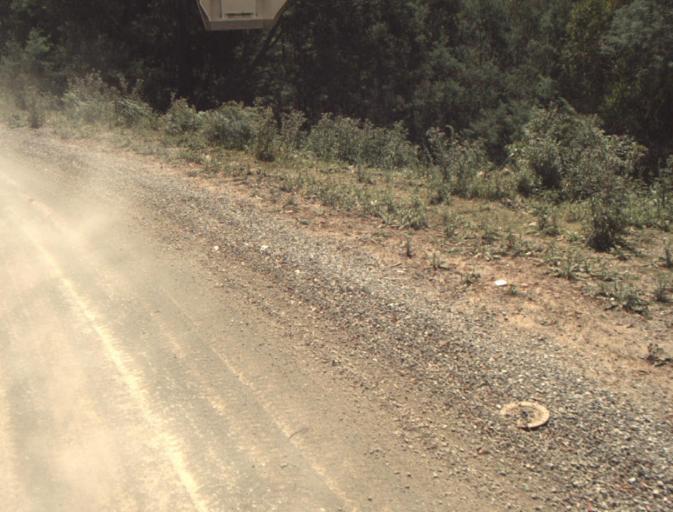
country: AU
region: Tasmania
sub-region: Dorset
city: Scottsdale
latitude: -41.3290
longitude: 147.4269
